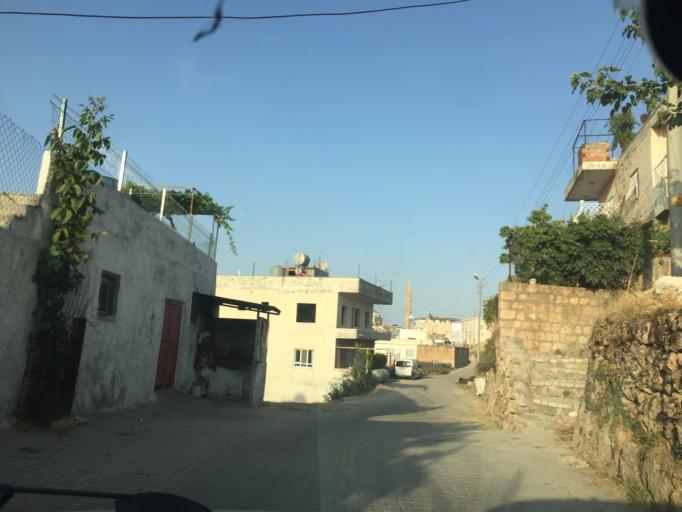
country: TR
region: Mardin
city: Kindirip
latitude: 37.4454
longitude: 41.2154
